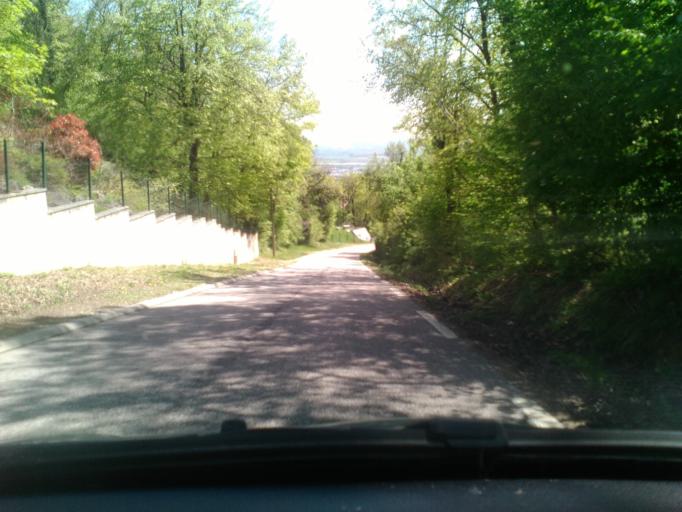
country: FR
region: Lorraine
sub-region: Departement de Meurthe-et-Moselle
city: Ludres
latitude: 48.6278
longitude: 6.1598
